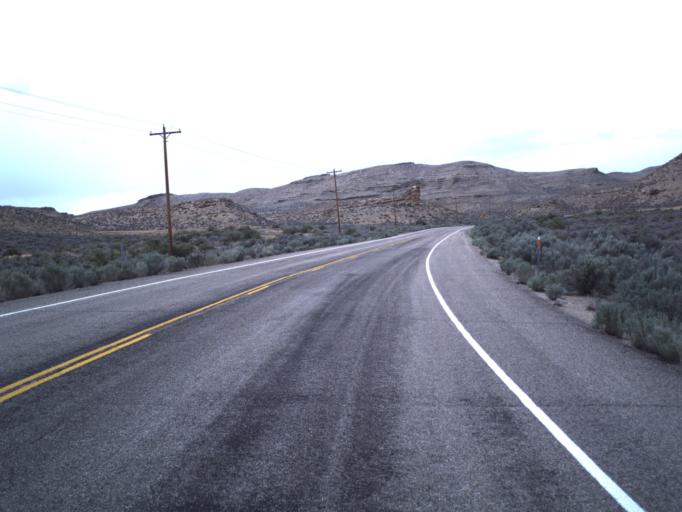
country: US
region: Colorado
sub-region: Rio Blanco County
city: Rangely
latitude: 39.9940
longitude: -109.1783
